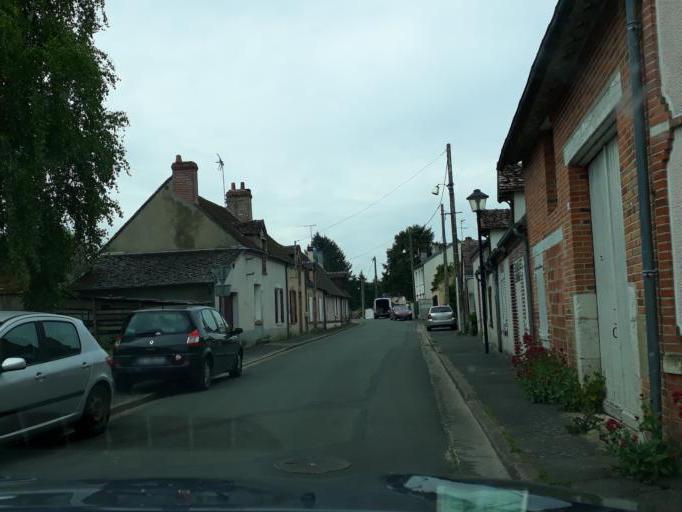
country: FR
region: Centre
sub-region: Departement du Loir-et-Cher
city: Dhuizon
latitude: 47.6528
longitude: 1.6715
